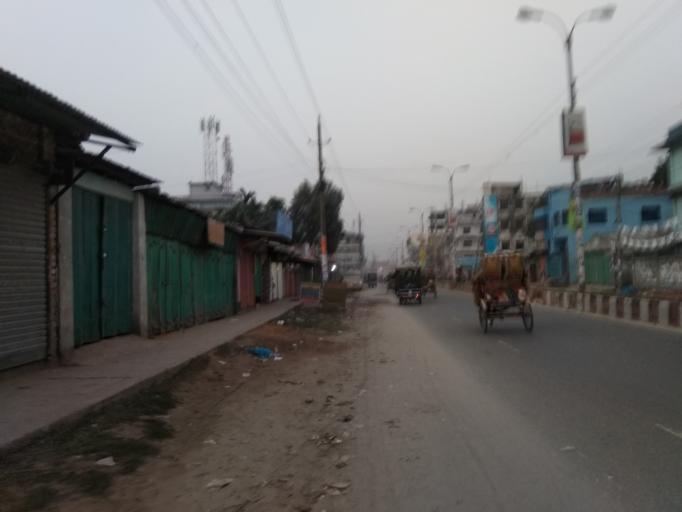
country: BD
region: Rangpur Division
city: Rangpur
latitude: 25.7312
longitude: 89.2547
